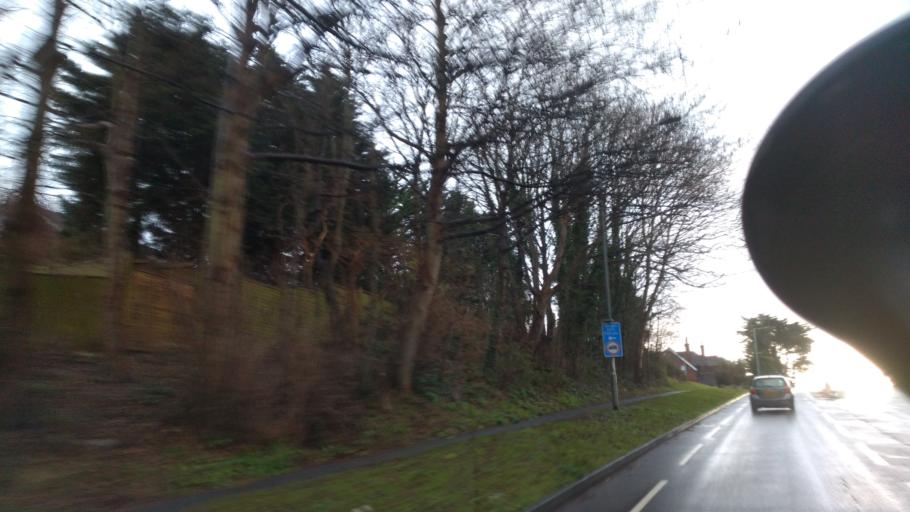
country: GB
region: England
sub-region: East Sussex
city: Eastbourne
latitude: 50.8008
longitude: 0.2543
